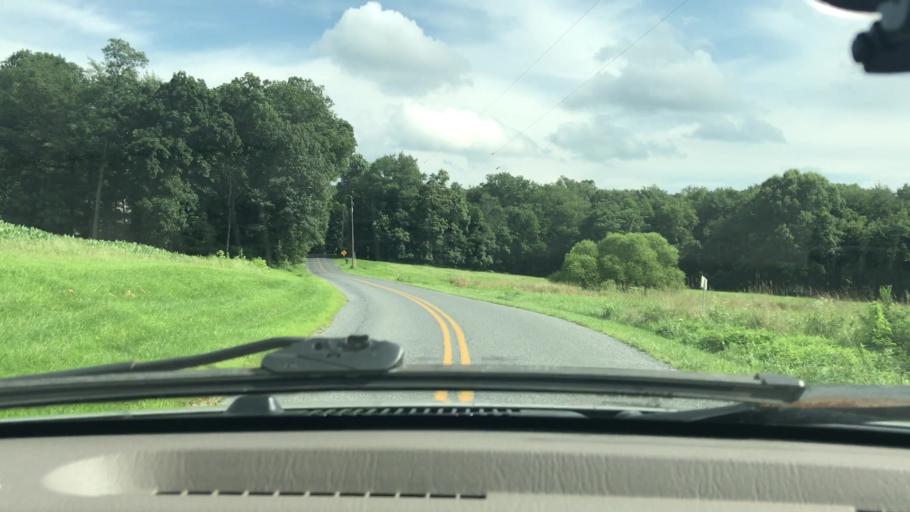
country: US
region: Pennsylvania
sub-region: Lancaster County
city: Elizabethtown
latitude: 40.1733
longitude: -76.6172
